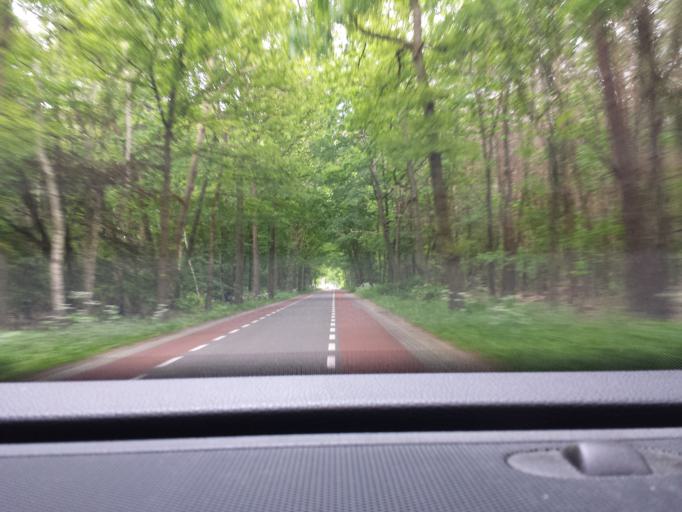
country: NL
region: Gelderland
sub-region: Gemeente Lochem
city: Lochem
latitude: 52.1393
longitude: 6.3869
